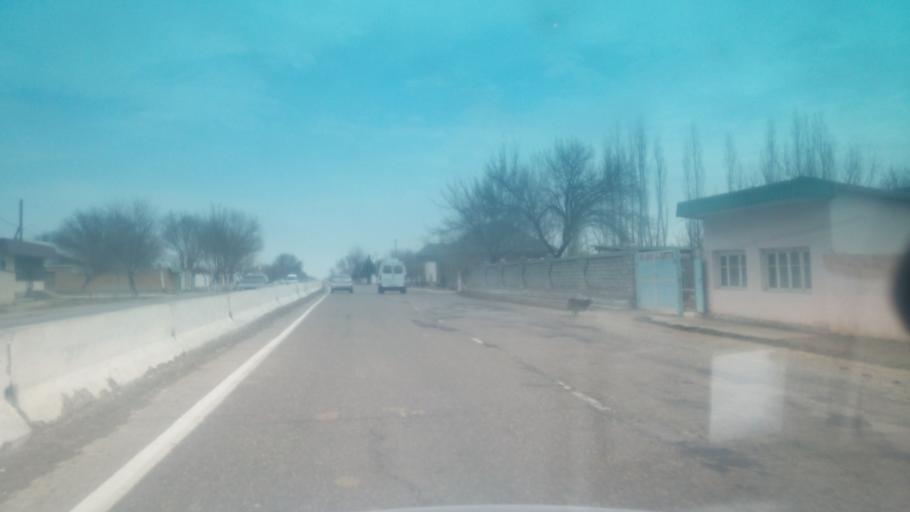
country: KZ
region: Ongtustik Qazaqstan
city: Myrzakent
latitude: 40.5004
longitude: 68.5579
